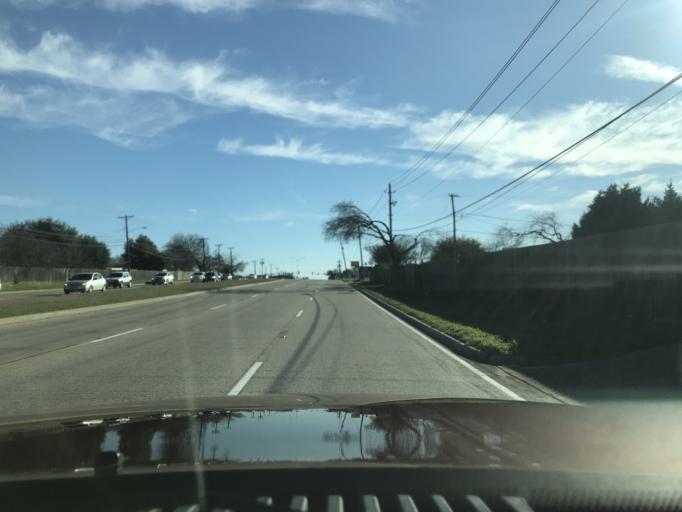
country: US
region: Texas
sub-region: Tarrant County
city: Edgecliff Village
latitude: 32.6519
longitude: -97.3486
